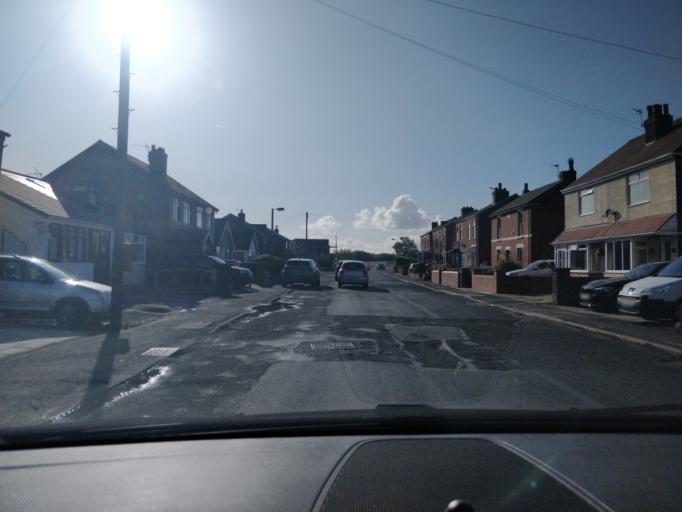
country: GB
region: England
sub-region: Lancashire
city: Banks
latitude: 53.6801
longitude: -2.9416
